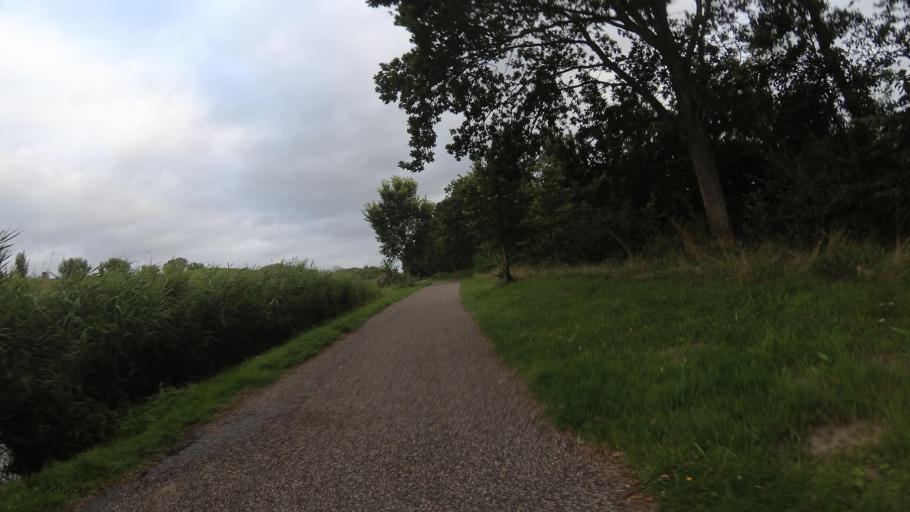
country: NL
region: North Holland
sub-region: Gemeente Den Helder
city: Den Helder
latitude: 52.9520
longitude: 4.7502
